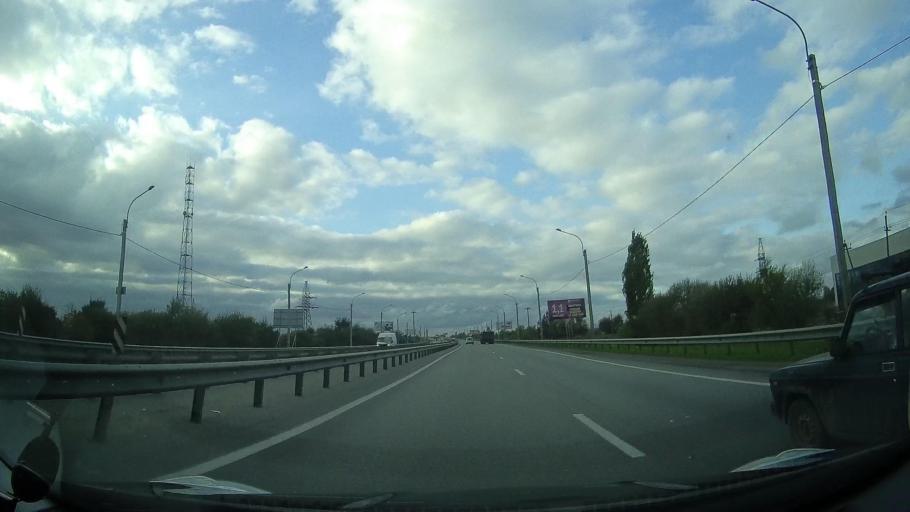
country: RU
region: Rostov
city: Bataysk
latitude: 47.1571
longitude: 39.7680
